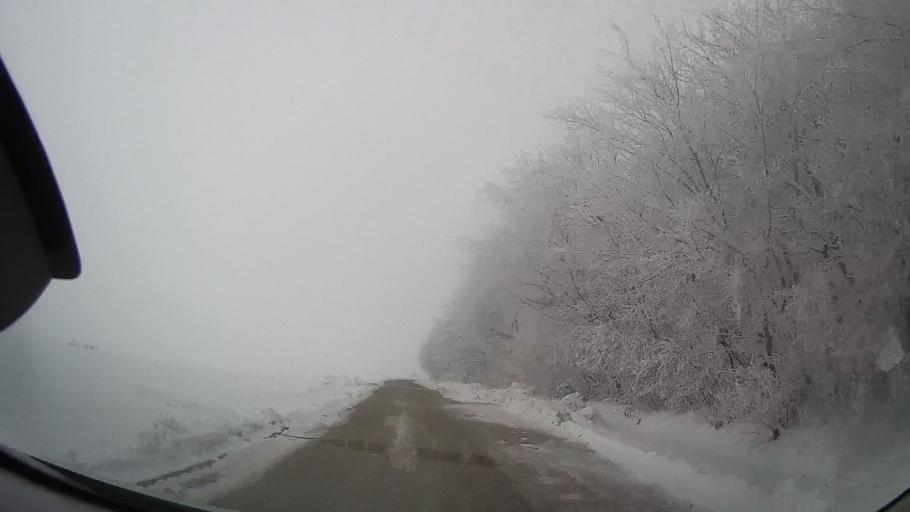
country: RO
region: Iasi
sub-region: Comuna Dagata
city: Dagata
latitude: 46.9111
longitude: 27.1833
